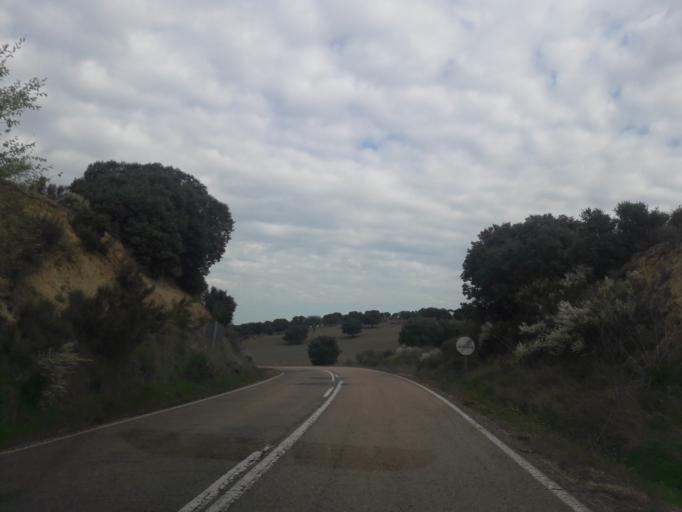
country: ES
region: Castille and Leon
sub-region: Provincia de Salamanca
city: Pastores
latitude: 40.5547
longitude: -6.5276
